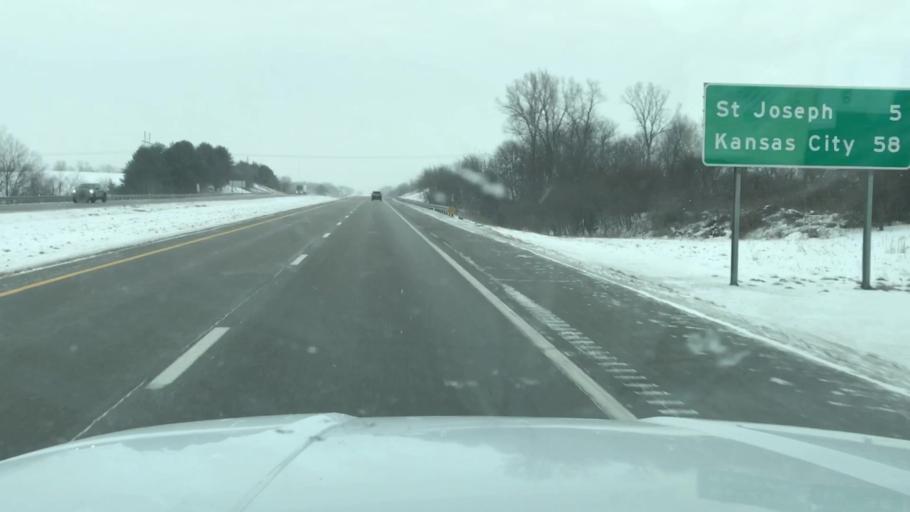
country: US
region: Missouri
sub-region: Andrew County
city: Country Club Village
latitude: 39.8475
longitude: -94.8054
